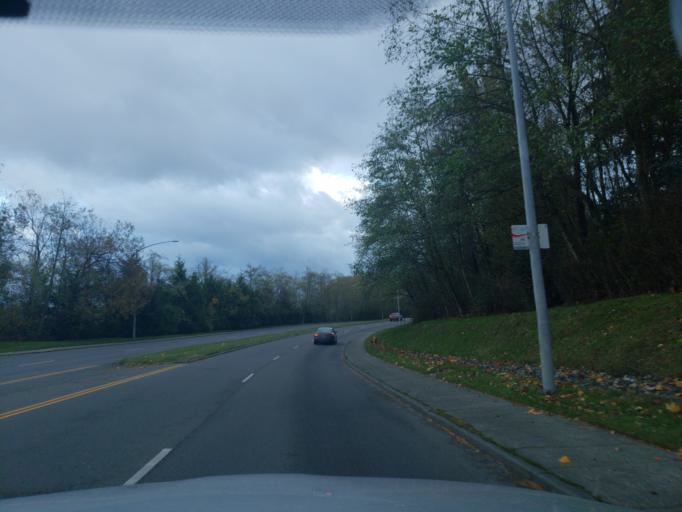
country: US
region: Washington
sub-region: Snohomish County
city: Mukilteo
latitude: 47.9342
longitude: -122.2613
